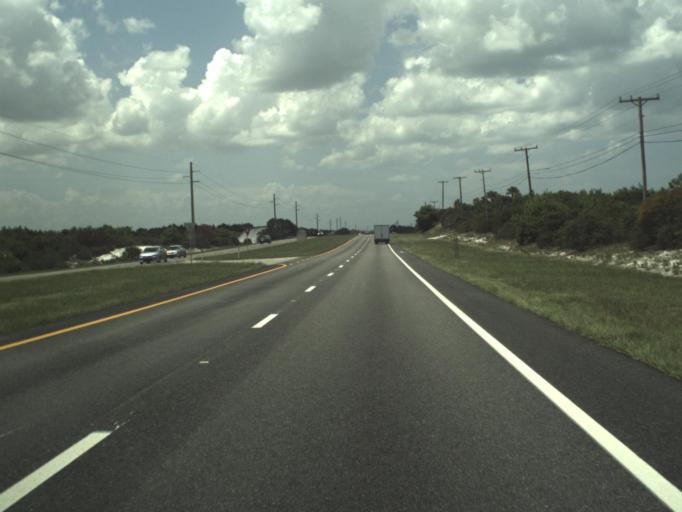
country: US
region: Florida
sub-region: Palm Beach County
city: Tequesta
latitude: 27.0125
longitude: -80.1037
